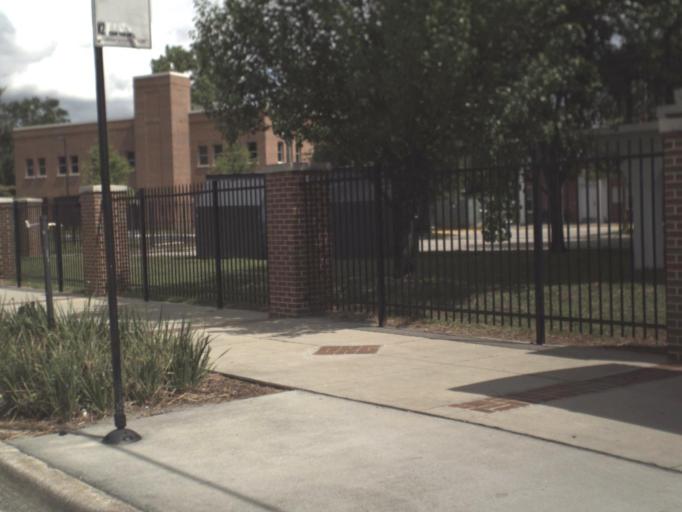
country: US
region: Florida
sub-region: Duval County
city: Jacksonville
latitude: 30.3446
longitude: -81.6851
